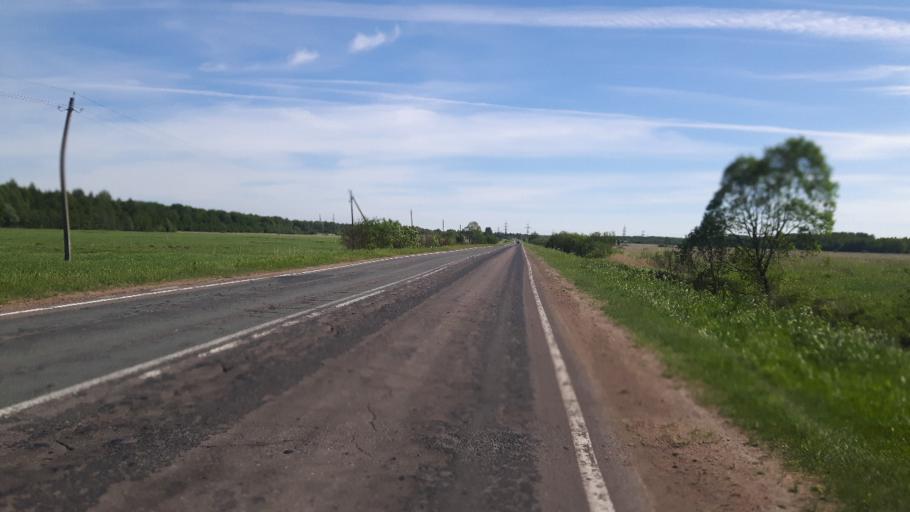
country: RU
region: Leningrad
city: Ivangorod
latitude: 59.4105
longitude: 28.3844
